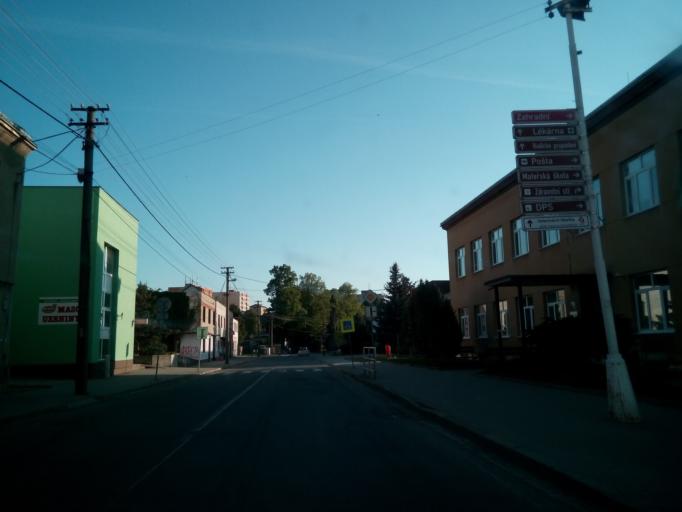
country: CZ
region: South Moravian
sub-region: Okres Blansko
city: Jedovnice
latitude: 49.3426
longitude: 16.7538
